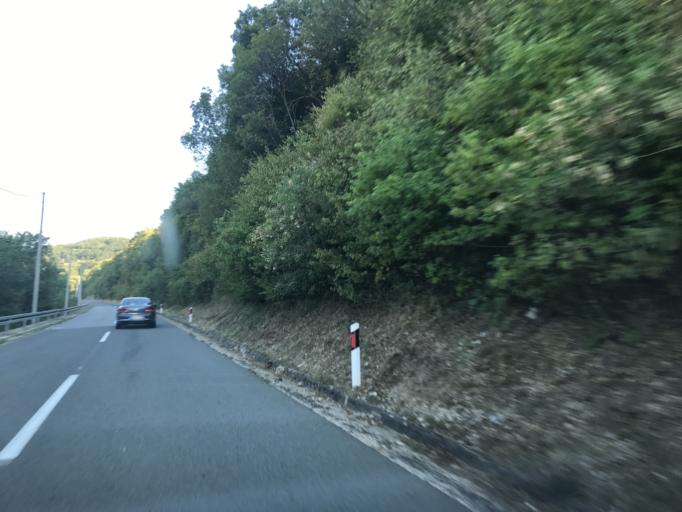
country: RO
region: Mehedinti
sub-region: Comuna Svinita
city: Svinita
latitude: 44.4811
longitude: 22.0922
